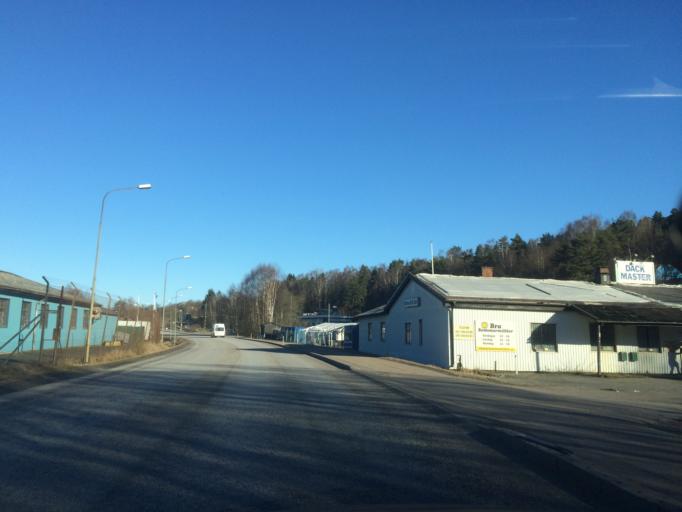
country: SE
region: Vaestra Goetaland
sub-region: Molndal
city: Kallered
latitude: 57.5979
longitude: 12.0592
